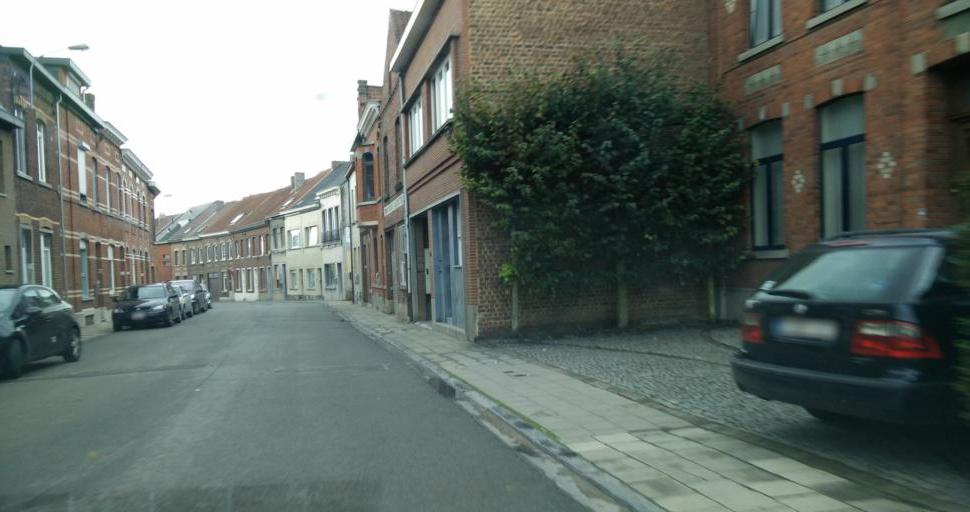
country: BE
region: Flanders
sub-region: Provincie Vlaams-Brabant
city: Halle
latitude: 50.7294
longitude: 4.2371
